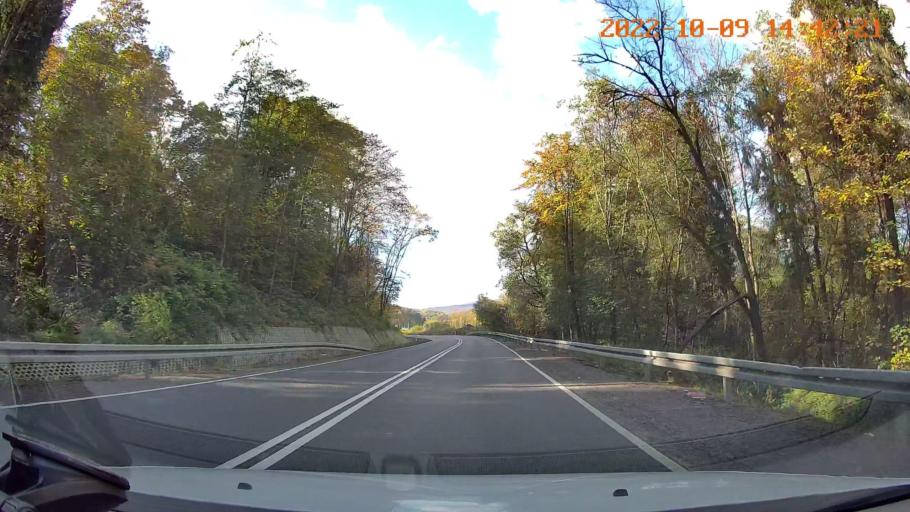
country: PL
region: Lesser Poland Voivodeship
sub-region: Powiat myslenicki
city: Lubien
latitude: 49.7136
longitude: 19.9985
